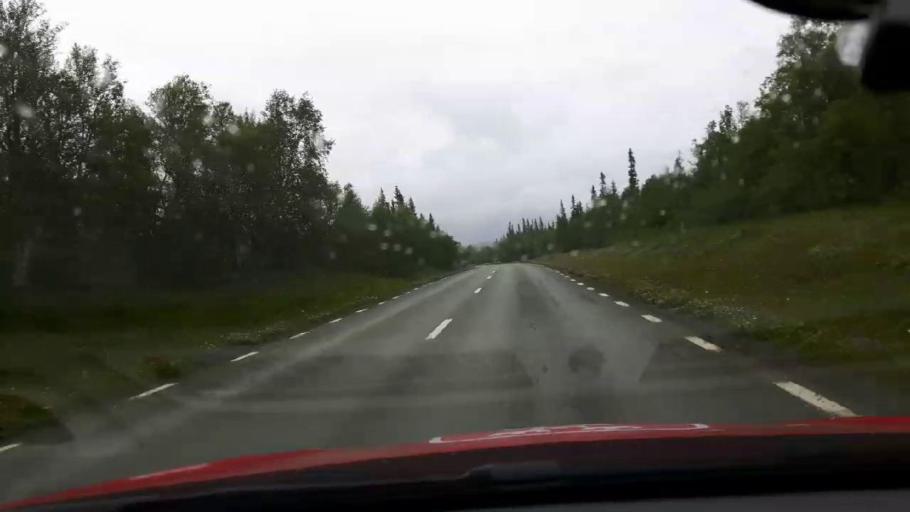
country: NO
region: Nord-Trondelag
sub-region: Meraker
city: Meraker
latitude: 63.2740
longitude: 12.1471
